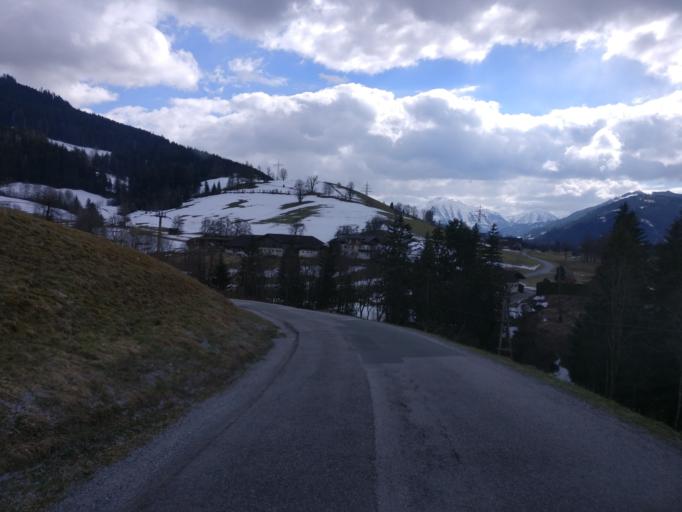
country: AT
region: Salzburg
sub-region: Politischer Bezirk Sankt Johann im Pongau
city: Bischofshofen
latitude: 47.4226
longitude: 13.2343
